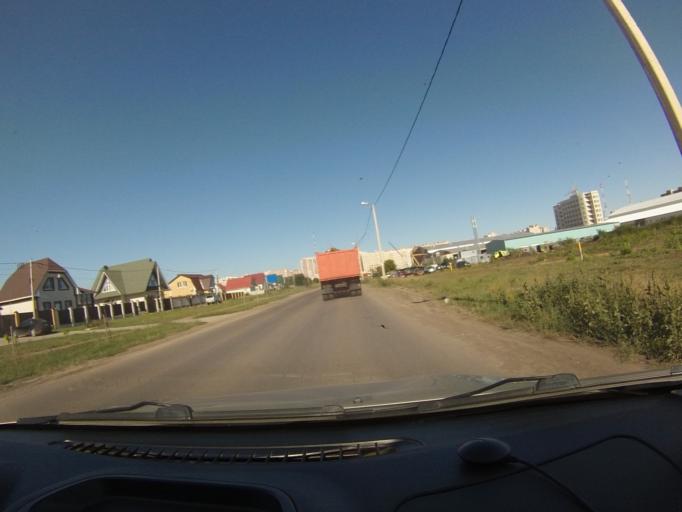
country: RU
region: Tambov
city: Tambov
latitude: 52.7662
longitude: 41.3869
